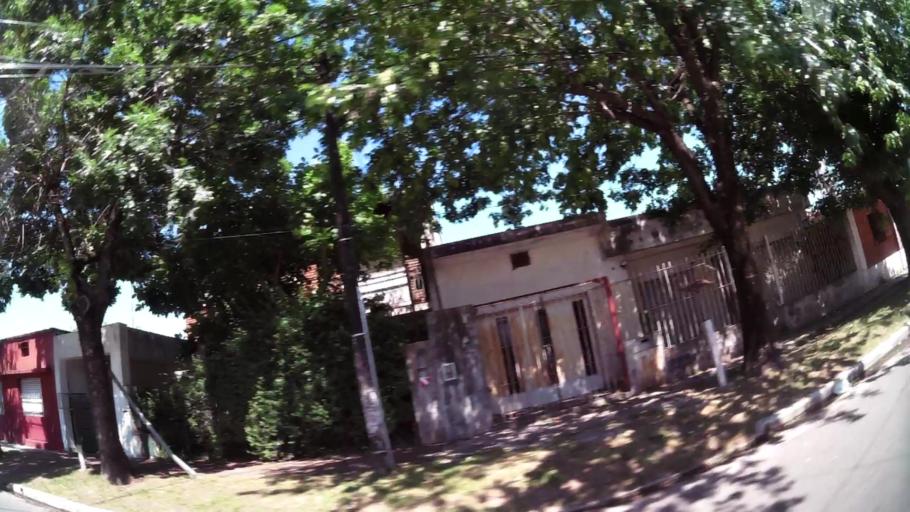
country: AR
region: Buenos Aires
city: Hurlingham
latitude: -34.5013
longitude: -58.6688
